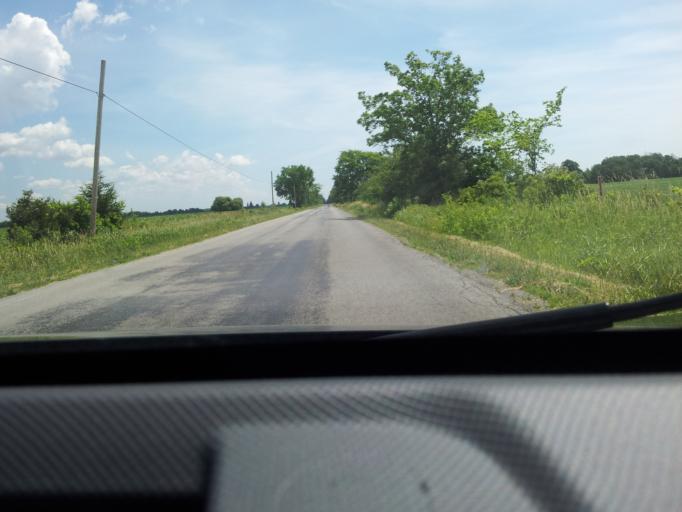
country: CA
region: Ontario
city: Norfolk County
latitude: 42.8260
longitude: -80.2712
